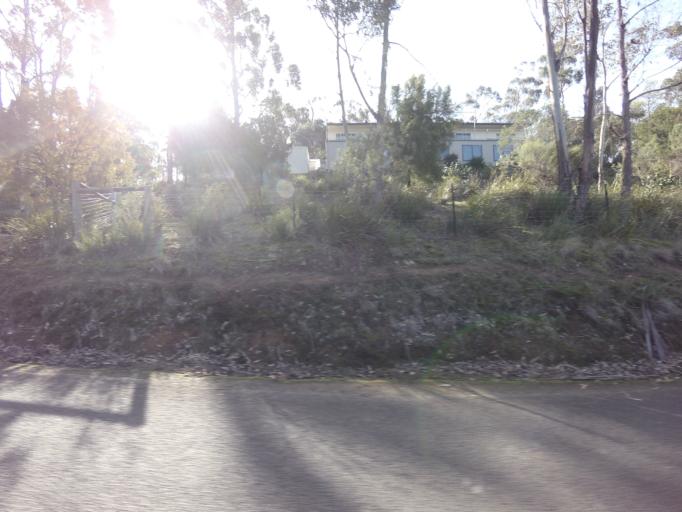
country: AU
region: Tasmania
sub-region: Kingborough
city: Kettering
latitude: -43.1214
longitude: 147.2538
